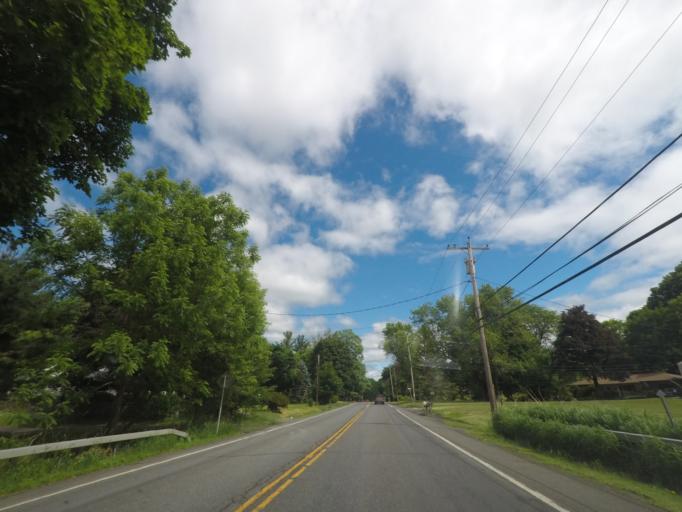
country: US
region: New York
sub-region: Columbia County
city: Philmont
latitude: 42.2232
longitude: -73.7149
